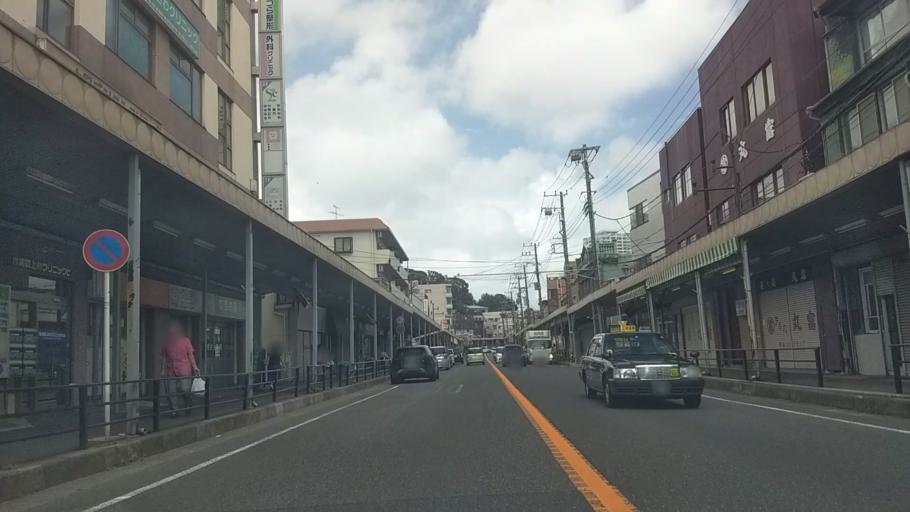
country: JP
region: Kanagawa
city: Yokosuka
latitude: 35.2738
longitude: 139.6702
